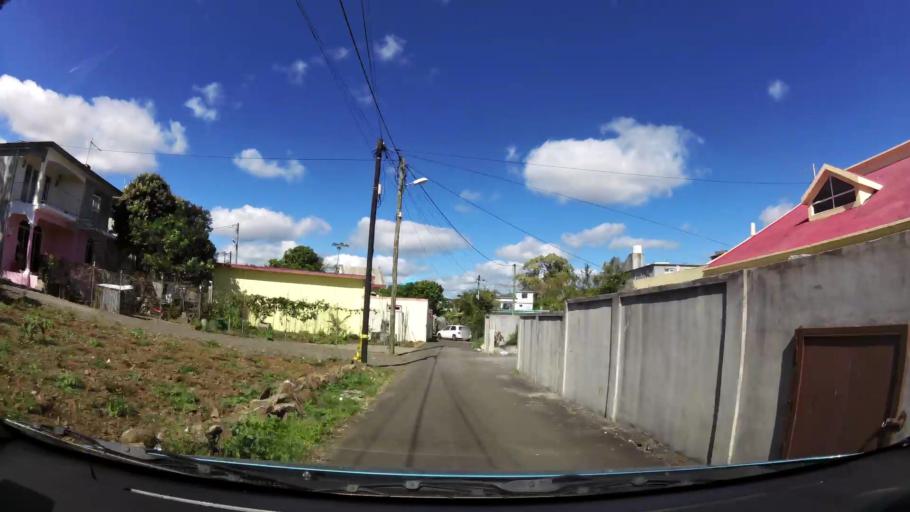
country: MU
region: Plaines Wilhems
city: Vacoas
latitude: -20.2927
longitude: 57.4769
